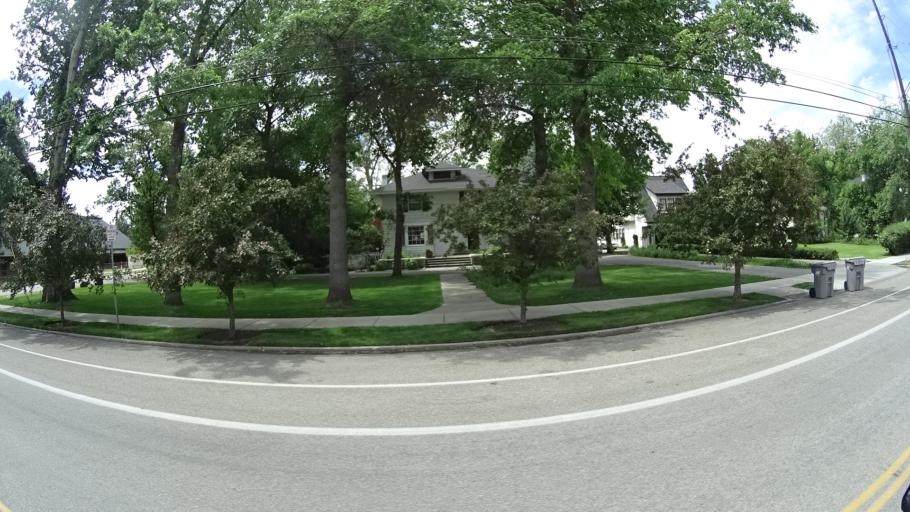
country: US
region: Idaho
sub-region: Ada County
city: Boise
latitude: 43.6037
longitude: -116.1747
